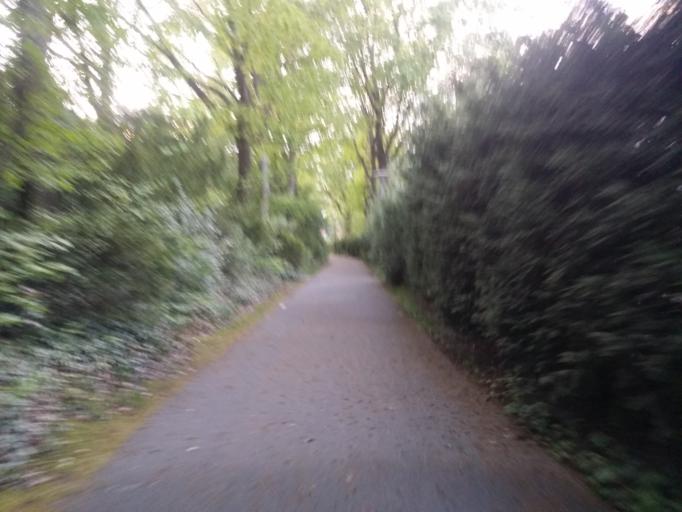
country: DE
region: Lower Saxony
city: Stuhr
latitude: 53.0382
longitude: 8.7300
